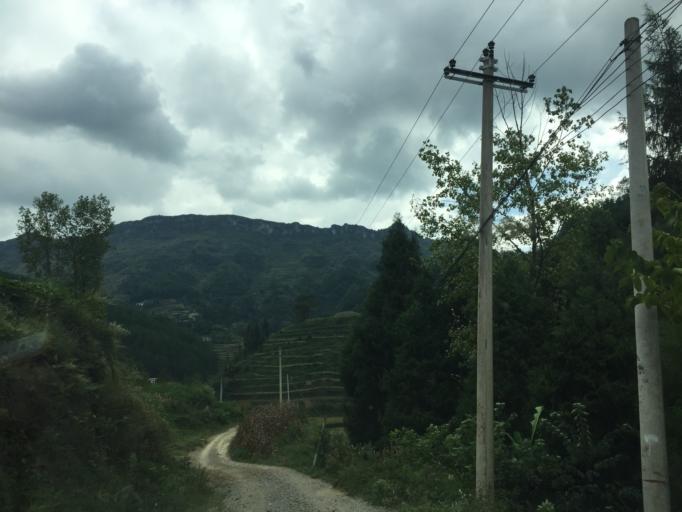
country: CN
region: Guizhou Sheng
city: Xujiaba
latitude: 27.9632
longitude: 108.1589
